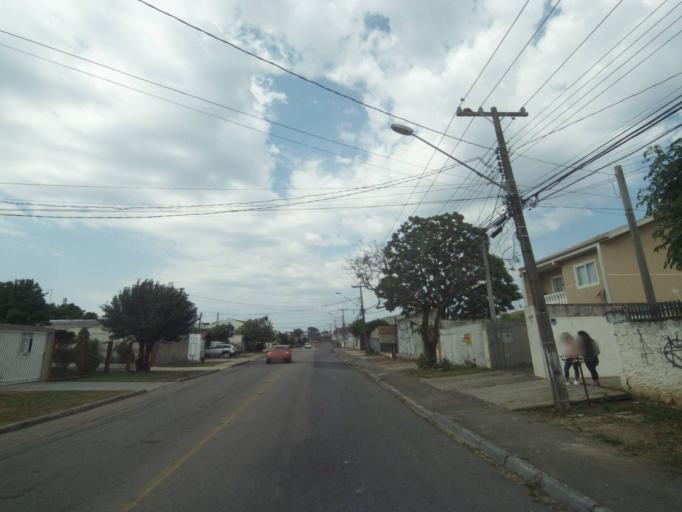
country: BR
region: Parana
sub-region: Sao Jose Dos Pinhais
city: Sao Jose dos Pinhais
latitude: -25.5226
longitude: -49.2656
